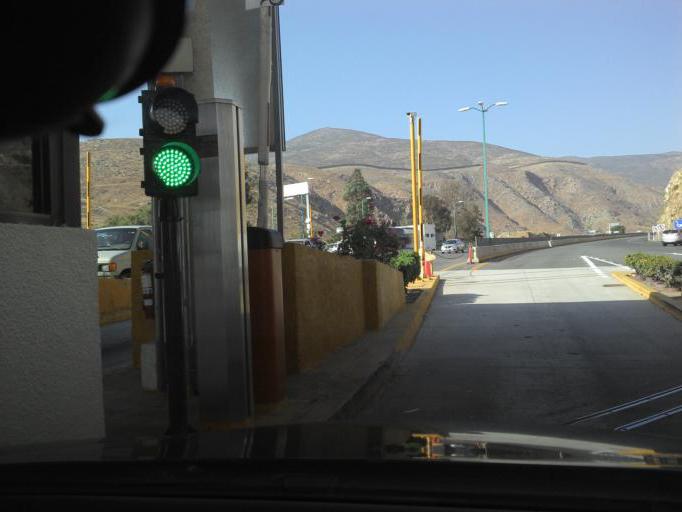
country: MX
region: Baja California
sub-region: Tijuana
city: Ejido Javier Rojo Gomez
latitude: 32.5457
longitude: -116.8522
